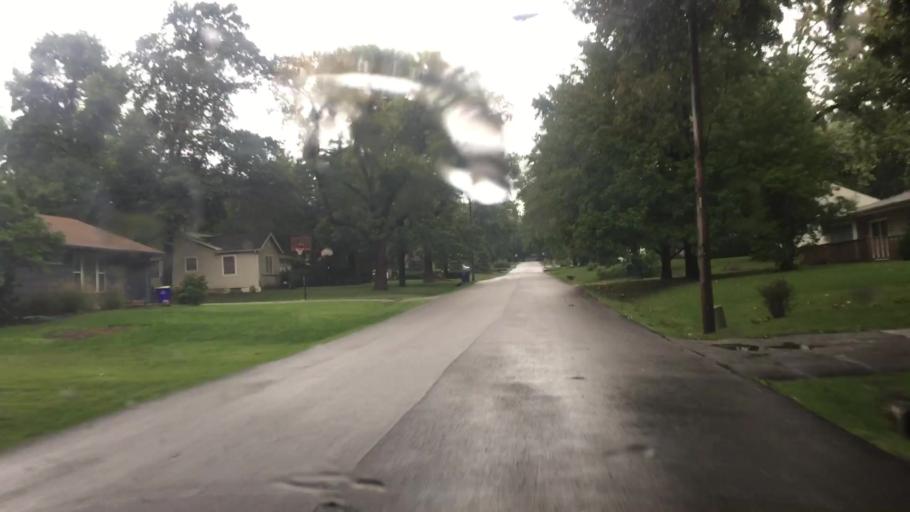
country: US
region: Kansas
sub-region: Johnson County
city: Shawnee
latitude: 39.0240
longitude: -94.7303
